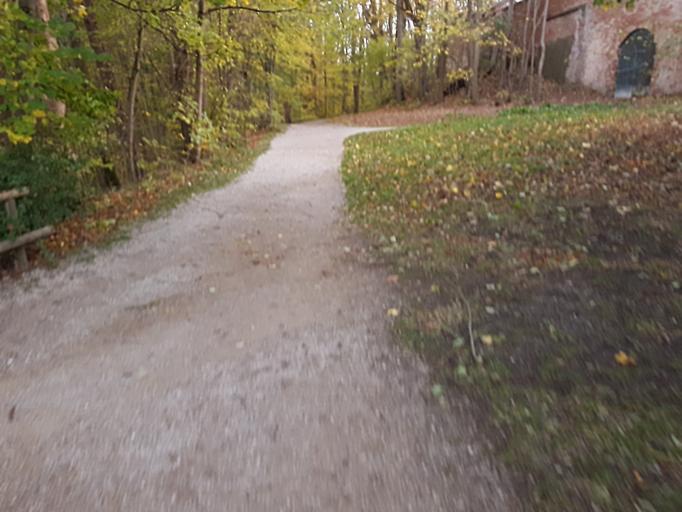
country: DE
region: Bavaria
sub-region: Lower Bavaria
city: Landshut
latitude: 48.5324
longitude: 12.1542
